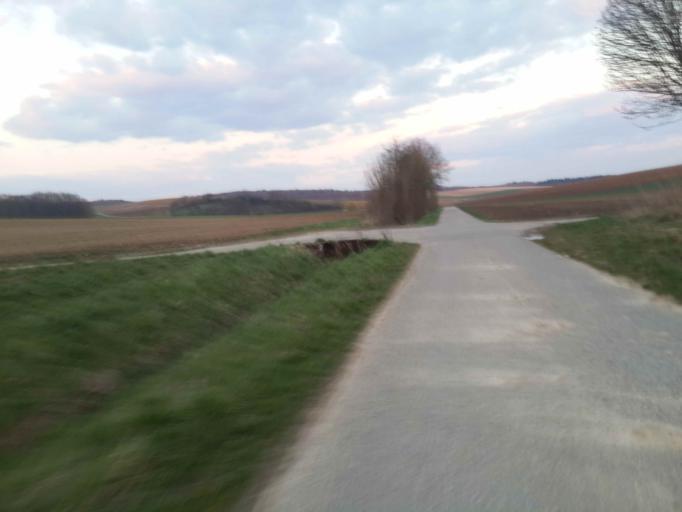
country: DE
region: Baden-Wuerttemberg
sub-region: Regierungsbezirk Stuttgart
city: Bad Rappenau
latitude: 49.2218
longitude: 9.0901
